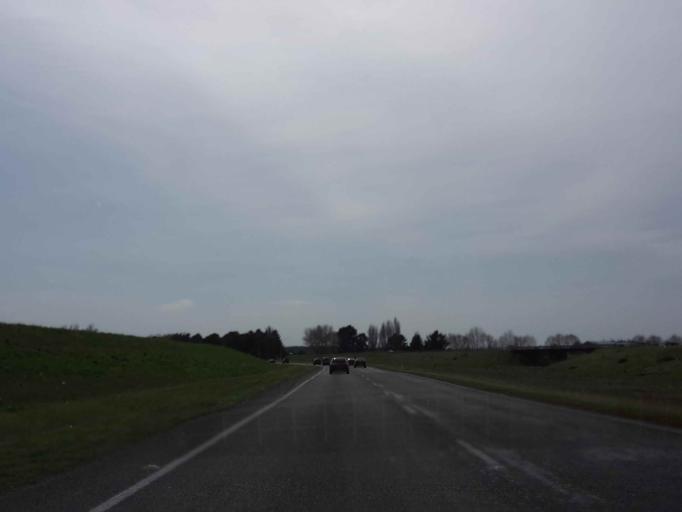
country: NZ
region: Canterbury
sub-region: Waimakariri District
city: Kaiapoi
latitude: -43.4310
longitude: 172.6430
